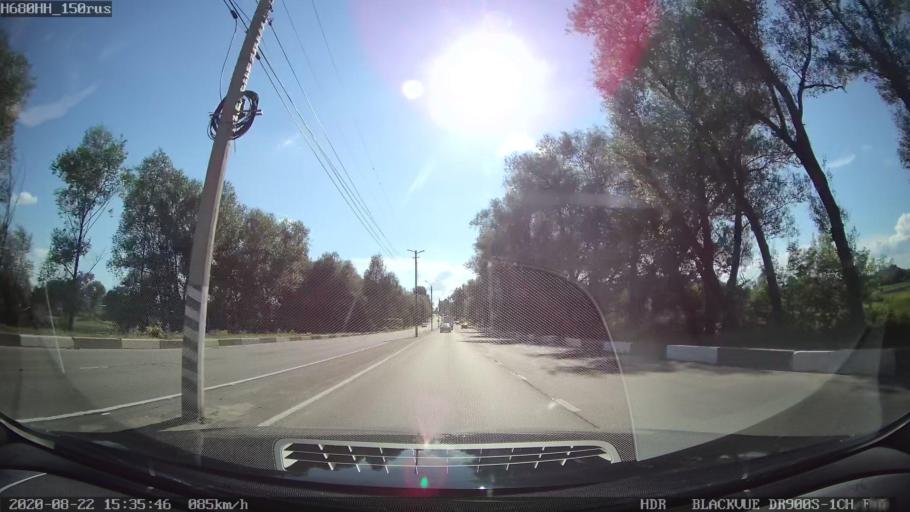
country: RU
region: Tverskaya
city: Bezhetsk
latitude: 57.7782
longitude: 36.6851
